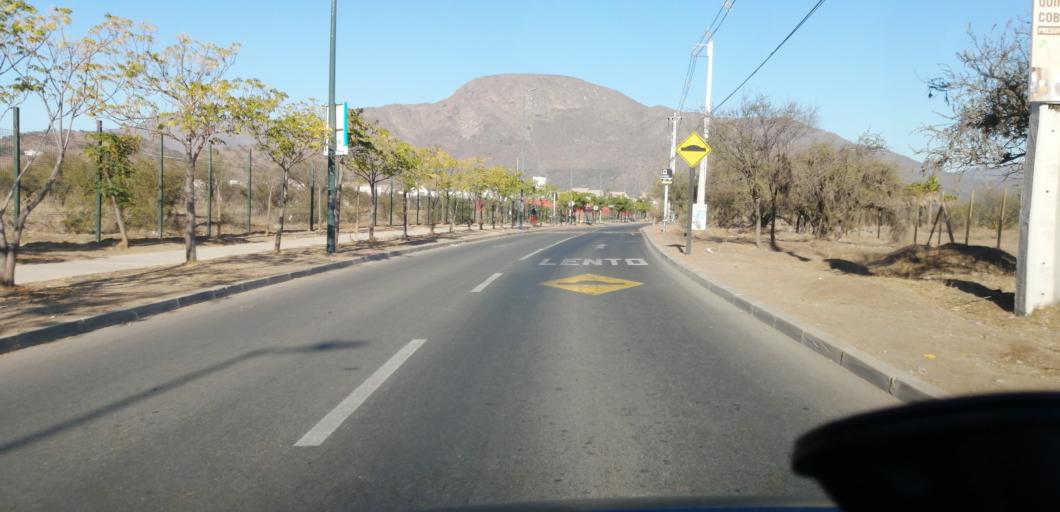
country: CL
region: Santiago Metropolitan
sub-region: Provincia de Santiago
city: Lo Prado
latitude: -33.4638
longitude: -70.8600
